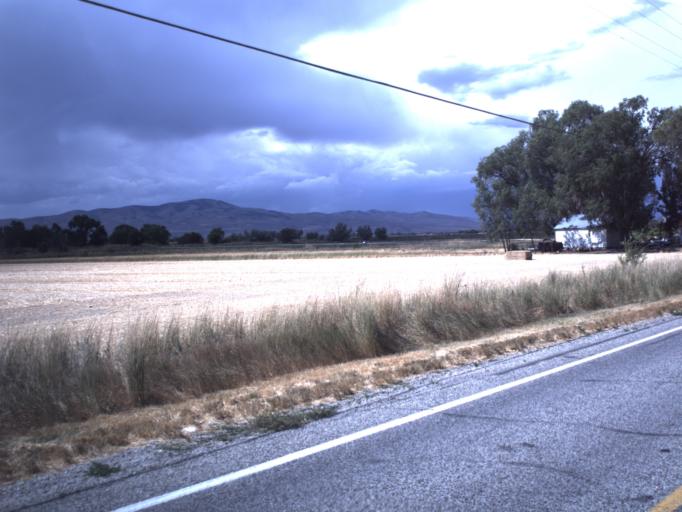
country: US
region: Utah
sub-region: Box Elder County
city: Honeyville
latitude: 41.6825
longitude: -112.0898
